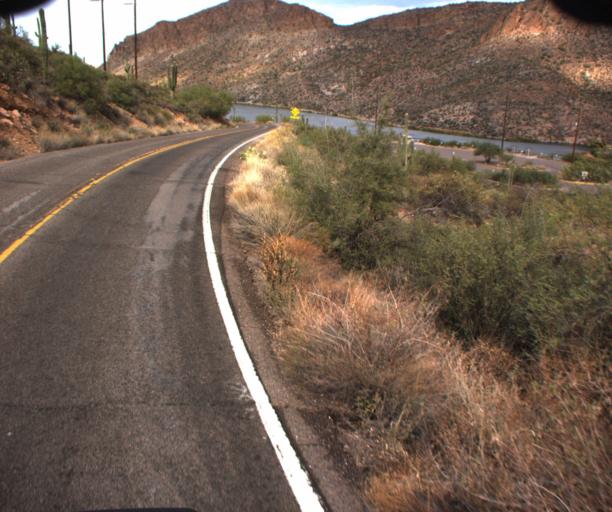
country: US
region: Arizona
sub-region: Pinal County
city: Apache Junction
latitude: 33.5315
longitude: -111.4157
